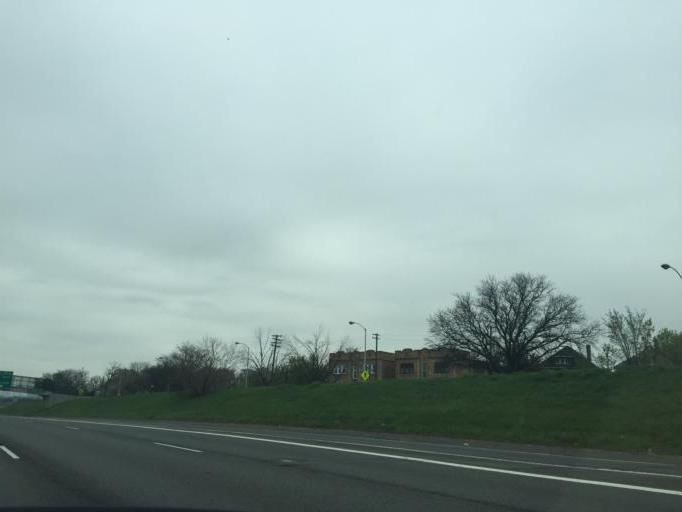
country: US
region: Michigan
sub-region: Wayne County
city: Highland Park
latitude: 42.3548
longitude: -83.1080
